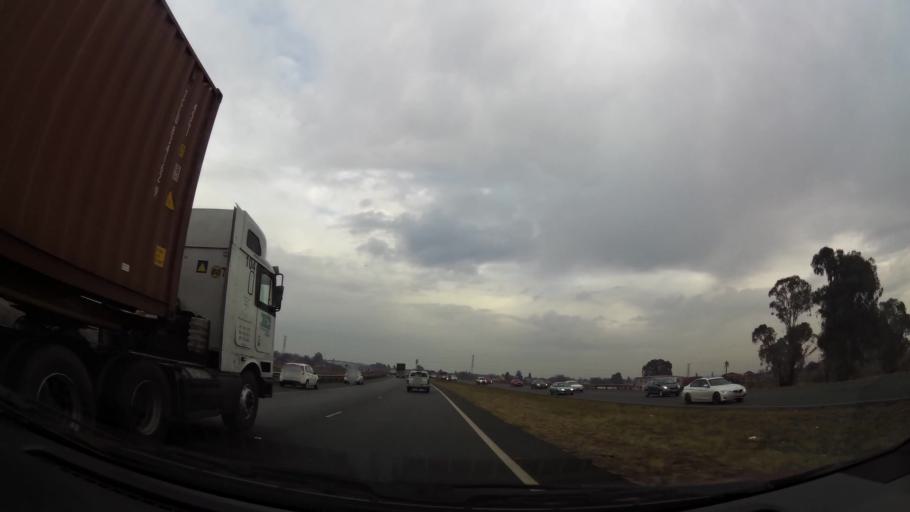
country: ZA
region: Gauteng
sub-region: City of Johannesburg Metropolitan Municipality
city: Soweto
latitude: -26.3027
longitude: 27.9053
